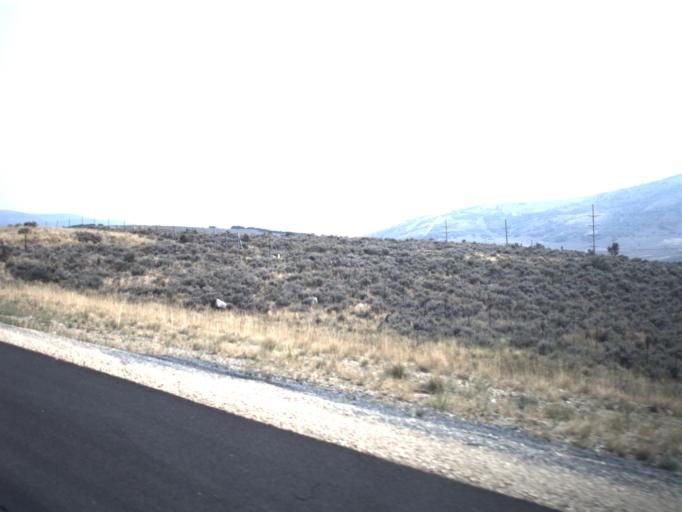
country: US
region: Utah
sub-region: Summit County
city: Park City
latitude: 40.6811
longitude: -111.4455
